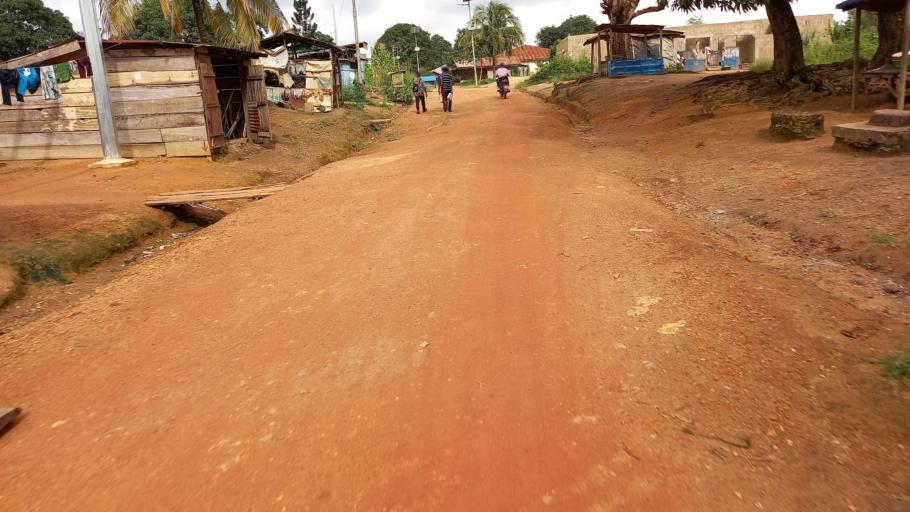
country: SL
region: Eastern Province
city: Kailahun
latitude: 8.2829
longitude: -10.5750
